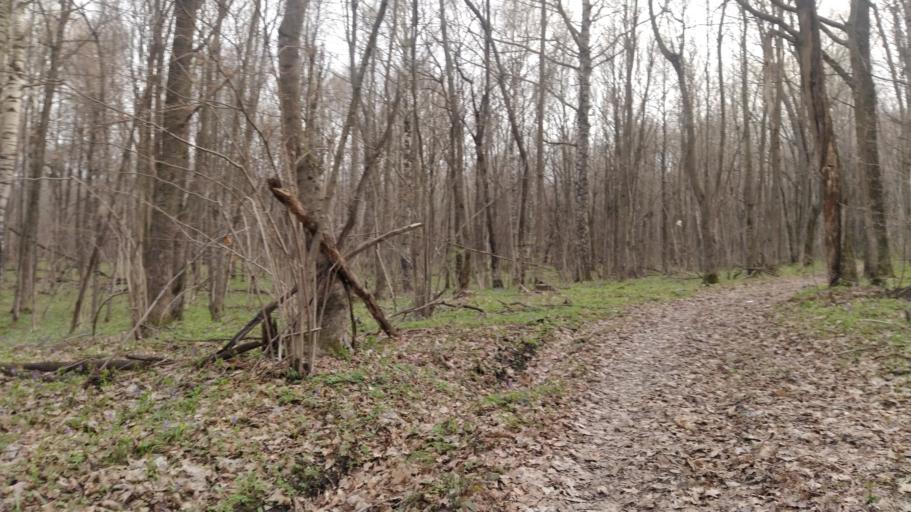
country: RU
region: Chuvashia
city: Novyye Lapsary
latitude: 56.1311
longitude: 47.1227
